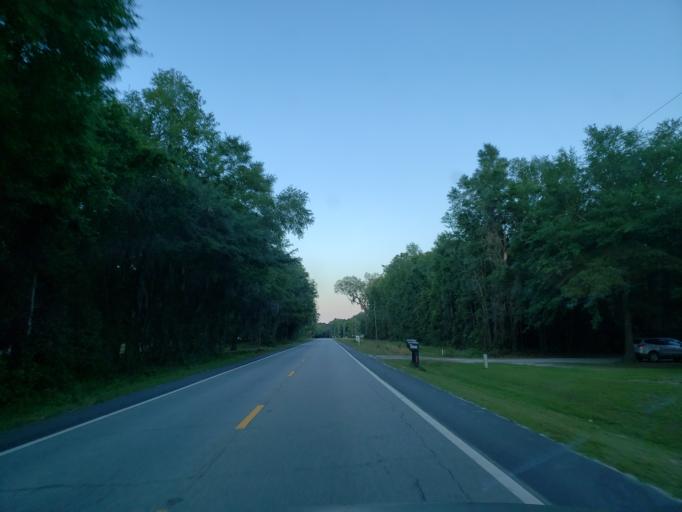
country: US
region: Florida
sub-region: Hamilton County
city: Jasper
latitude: 30.5549
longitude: -83.1140
